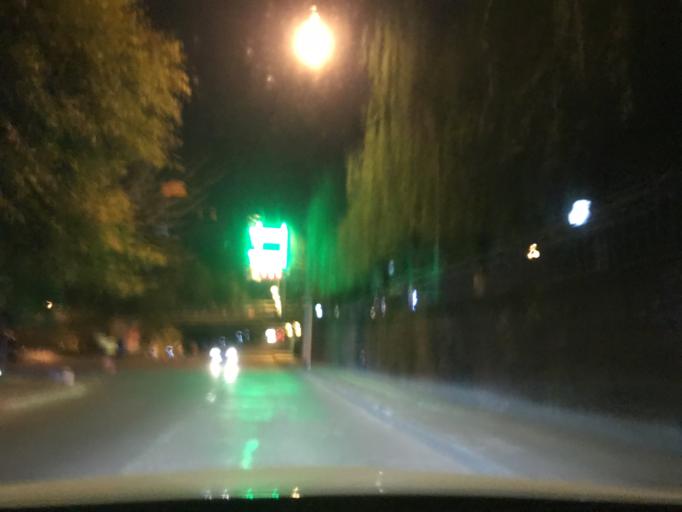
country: CN
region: Sichuan
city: Mianyang
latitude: 31.4555
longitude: 104.7465
